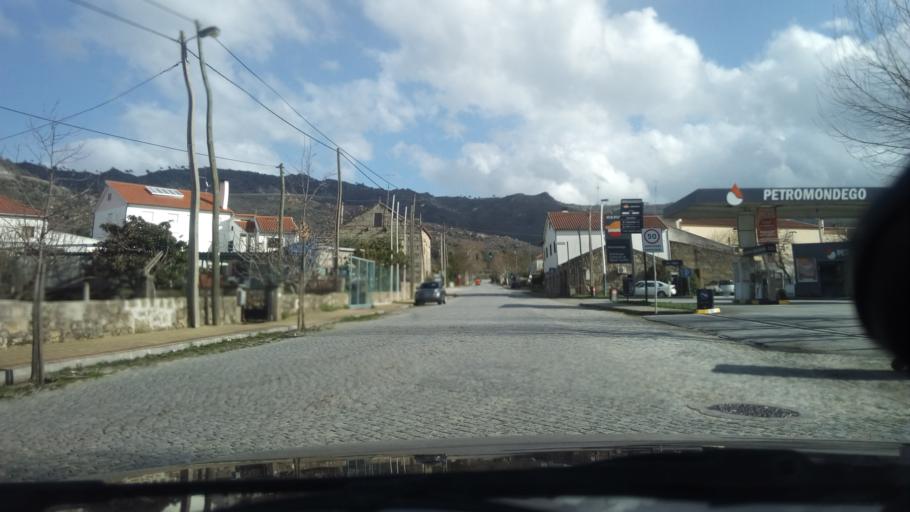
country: PT
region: Guarda
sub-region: Guarda
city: Guarda
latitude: 40.6039
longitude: -7.2972
